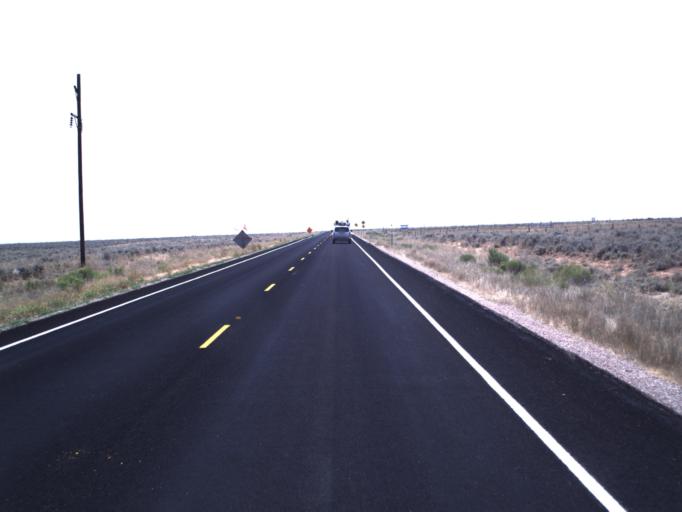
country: US
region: Utah
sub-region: Uintah County
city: Maeser
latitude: 40.4064
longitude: -109.7660
